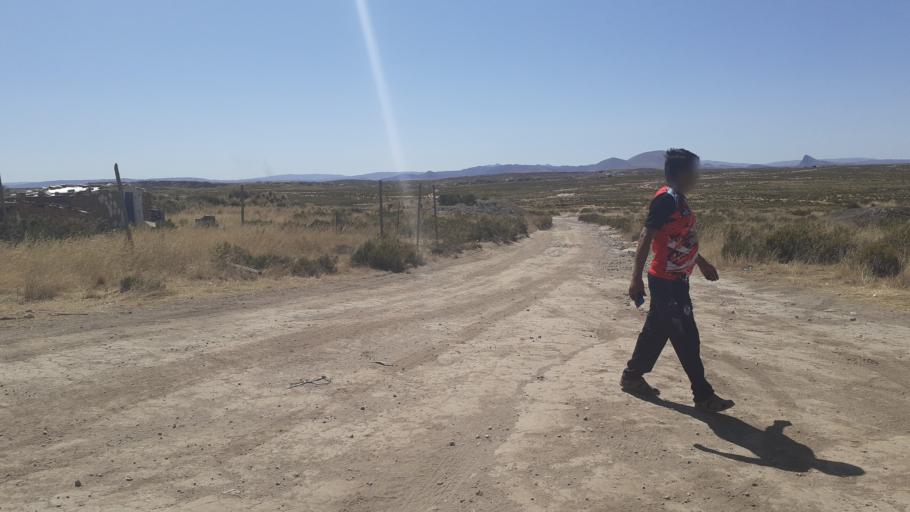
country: BO
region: La Paz
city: Tiahuanaco
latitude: -17.1114
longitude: -68.8100
